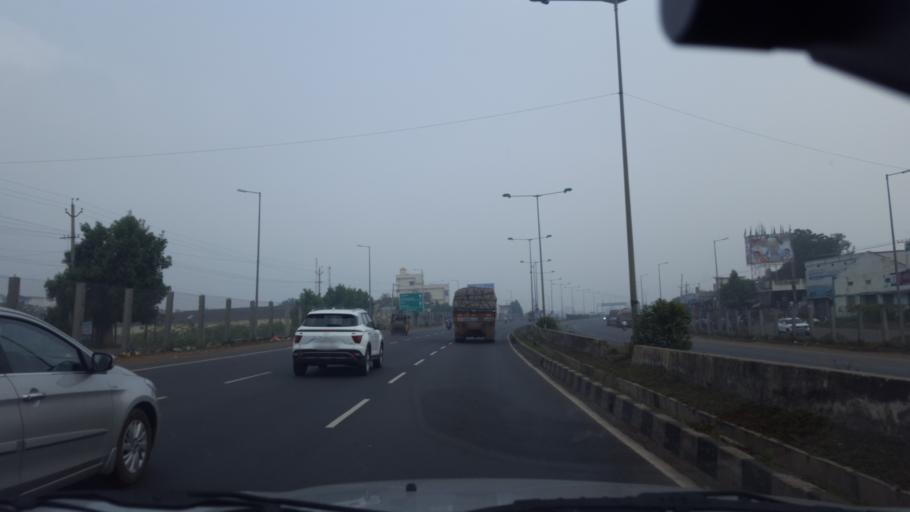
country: IN
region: Andhra Pradesh
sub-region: Prakasam
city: Ongole
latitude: 15.5437
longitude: 80.0523
